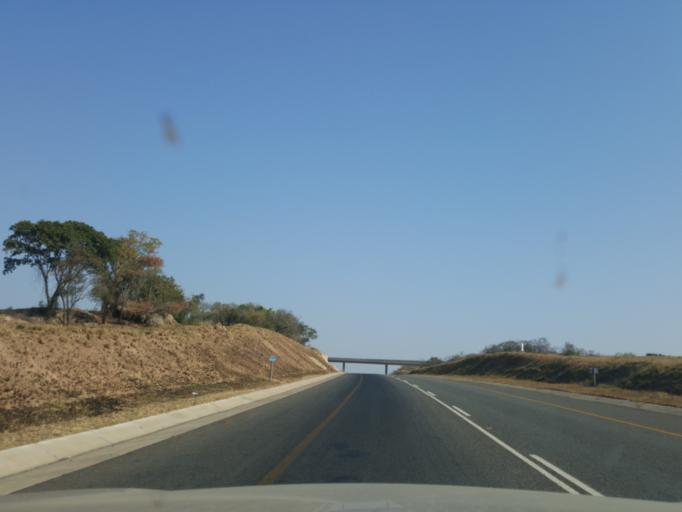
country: ZA
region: Mpumalanga
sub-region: Ehlanzeni District
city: Nelspruit
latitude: -25.4541
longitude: 31.0264
